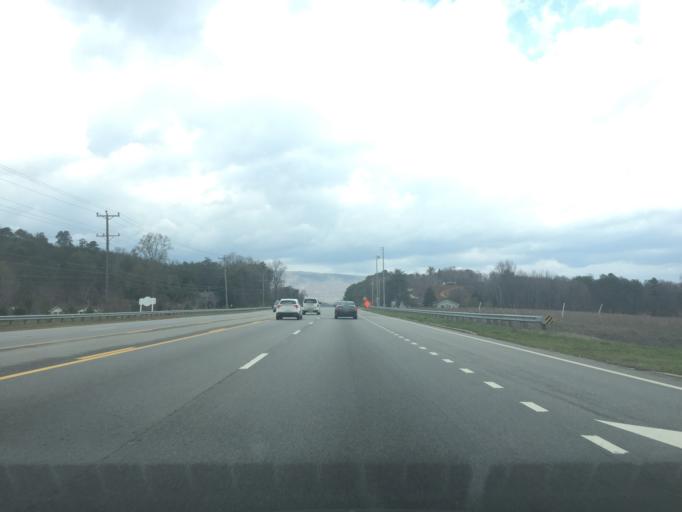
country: US
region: Tennessee
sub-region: Hamilton County
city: Falling Water
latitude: 35.1674
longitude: -85.2478
